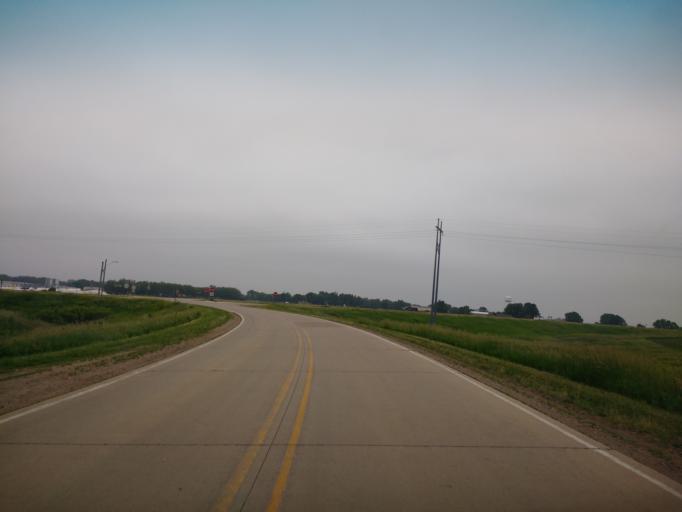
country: US
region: Iowa
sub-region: O'Brien County
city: Sheldon
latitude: 43.0610
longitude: -95.8997
